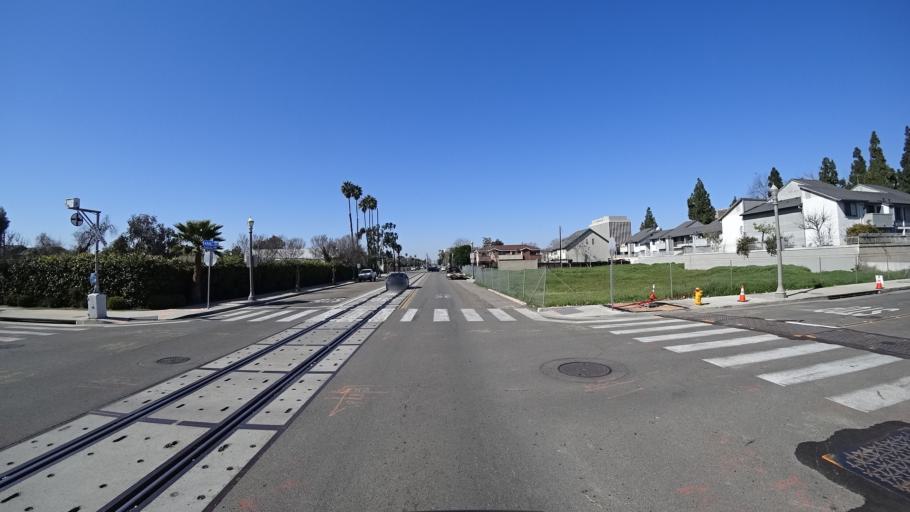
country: US
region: California
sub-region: Orange County
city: Anaheim
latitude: 33.8307
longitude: -117.9143
